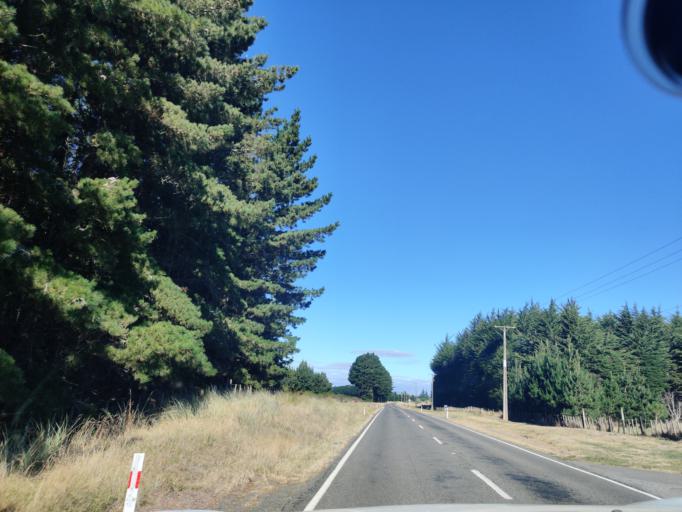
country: NZ
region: Manawatu-Wanganui
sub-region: Horowhenua District
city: Foxton
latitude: -40.3751
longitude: 175.2507
